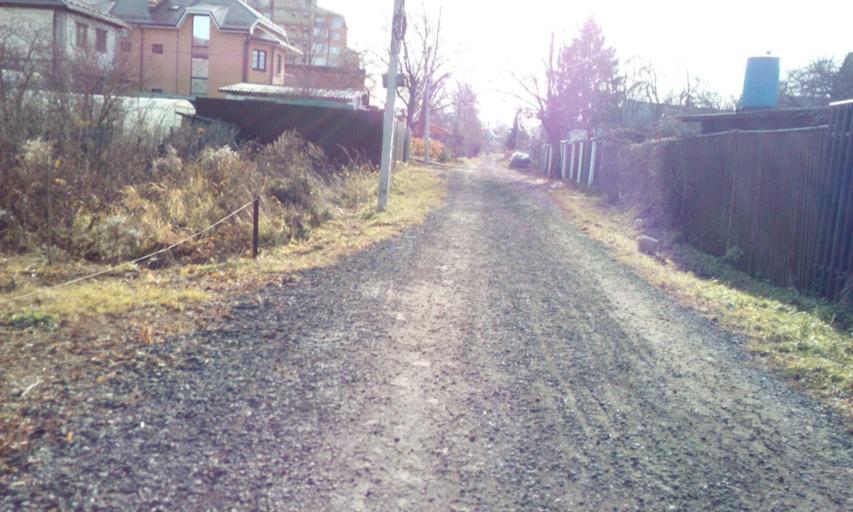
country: RU
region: Moskovskaya
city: Zhavoronki
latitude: 55.6574
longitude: 37.1526
